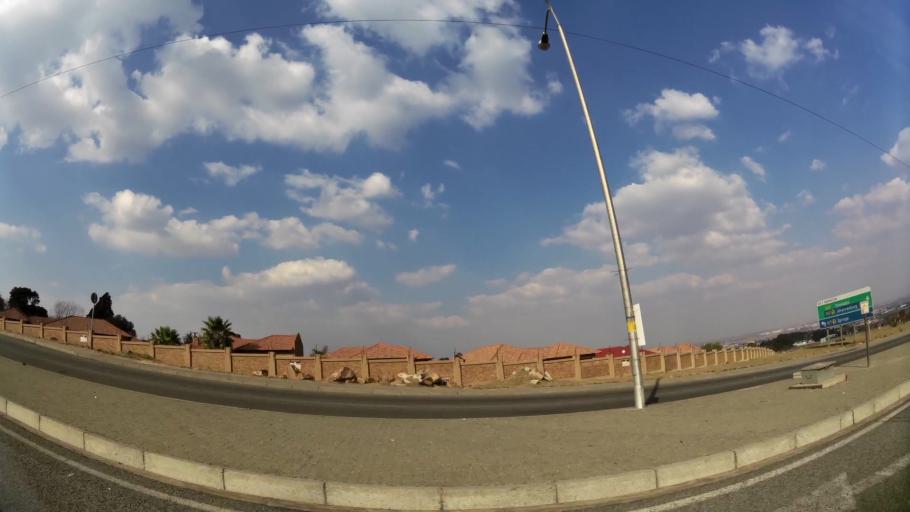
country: ZA
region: Gauteng
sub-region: Ekurhuleni Metropolitan Municipality
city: Germiston
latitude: -26.2449
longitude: 28.1649
